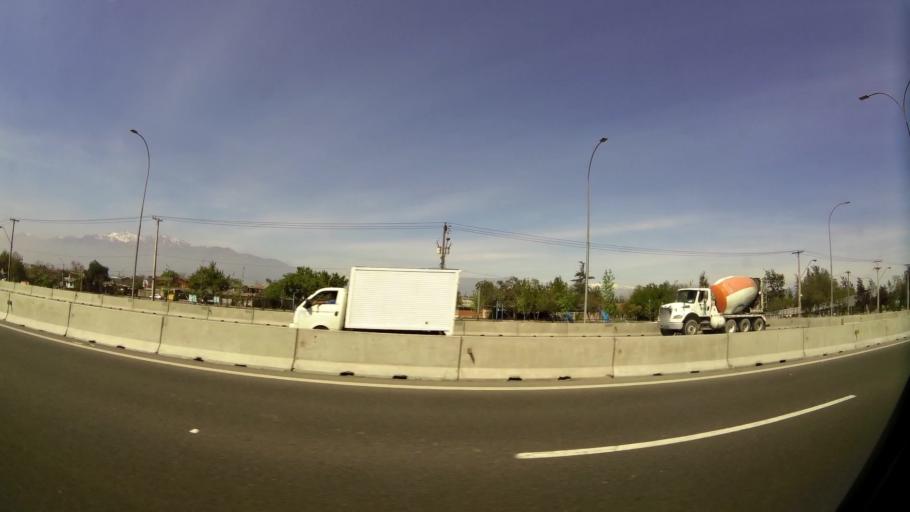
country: CL
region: Santiago Metropolitan
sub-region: Provincia de Maipo
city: San Bernardo
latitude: -33.5356
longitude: -70.6836
